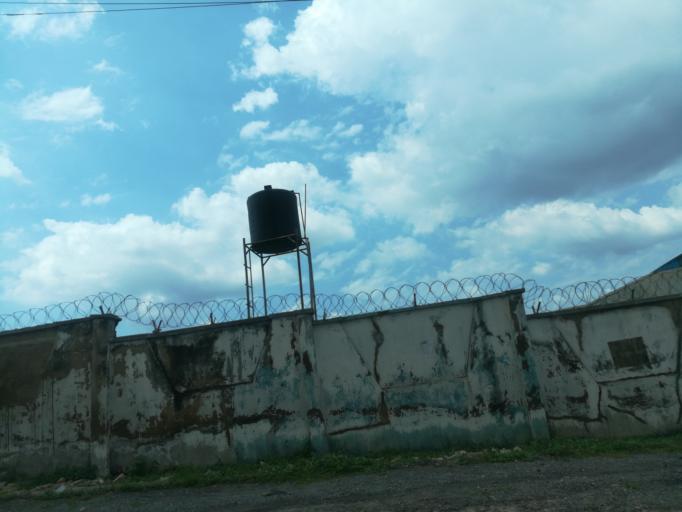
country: NG
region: Oyo
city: Ibadan
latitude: 7.4101
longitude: 3.8676
